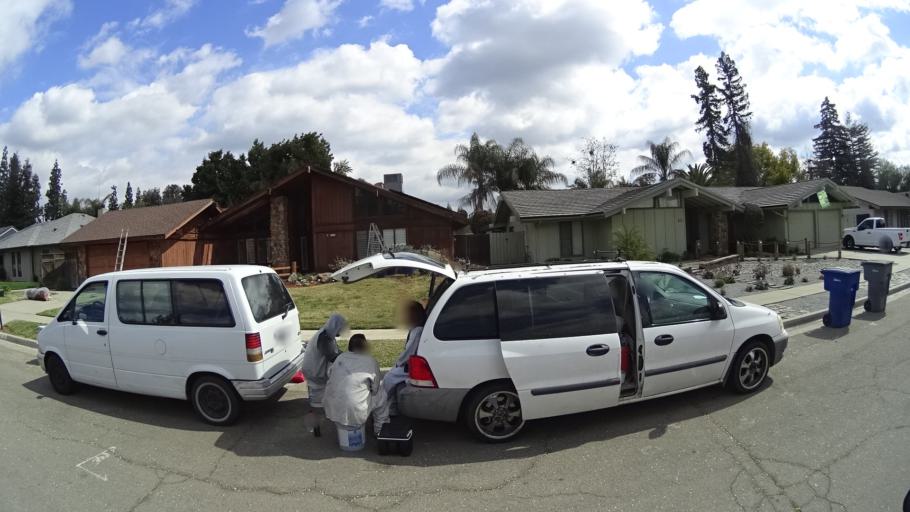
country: US
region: California
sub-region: Fresno County
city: Fresno
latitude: 36.8359
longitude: -119.8576
